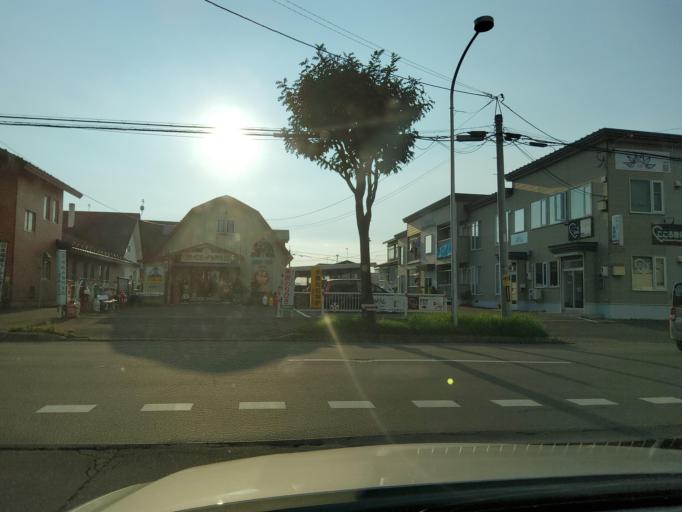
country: JP
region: Hokkaido
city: Obihiro
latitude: 42.9166
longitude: 143.1852
